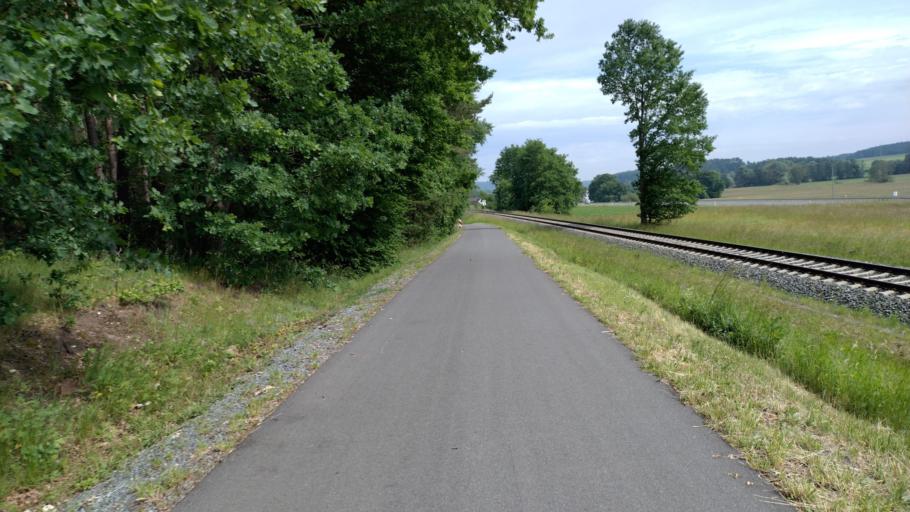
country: DE
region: Bavaria
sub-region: Upper Franconia
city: Harsdorf
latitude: 50.0135
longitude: 11.5827
